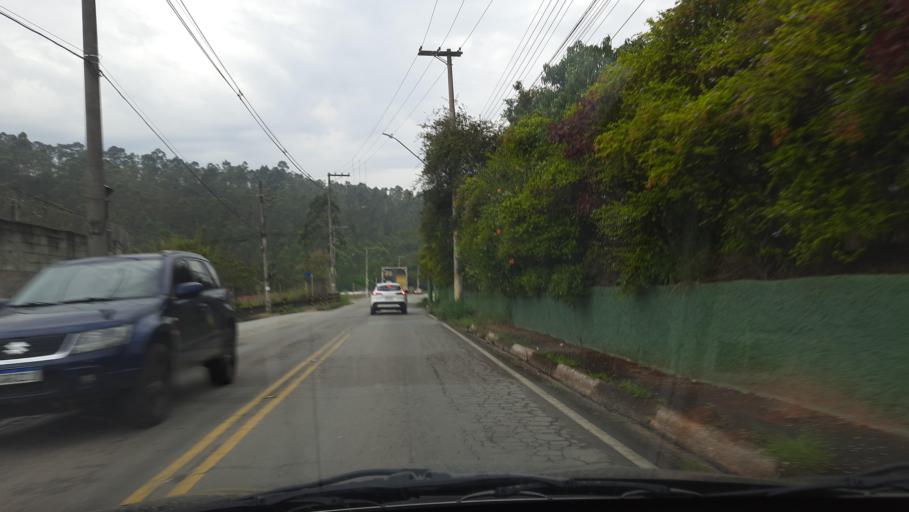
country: BR
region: Sao Paulo
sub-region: Caieiras
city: Caieiras
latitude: -23.3770
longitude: -46.7111
